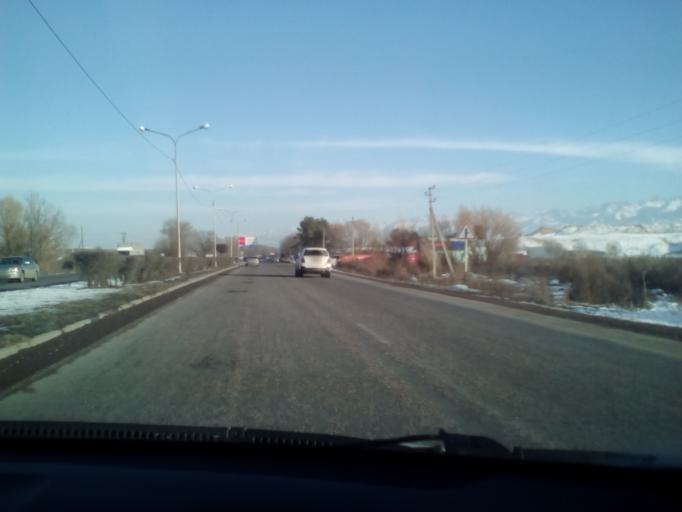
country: KZ
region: Almaty Oblysy
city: Burunday
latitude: 43.2224
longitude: 76.4244
